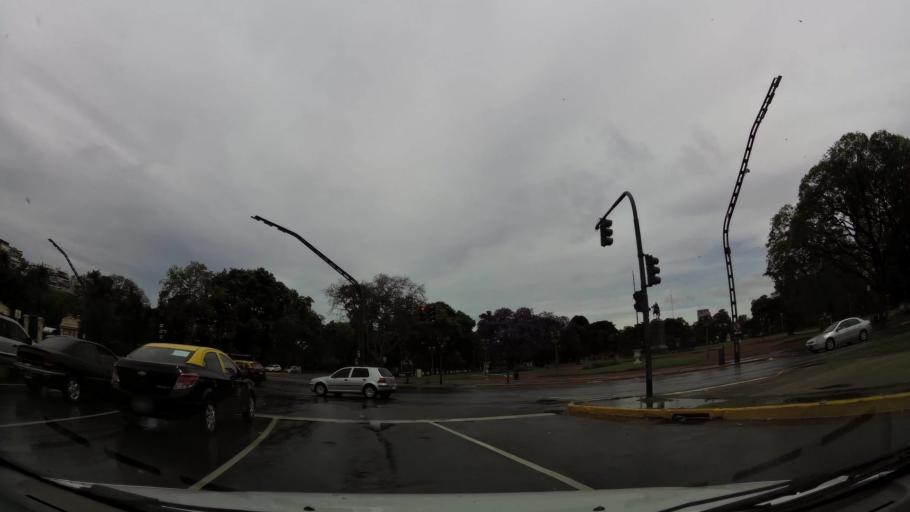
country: AR
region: Buenos Aires F.D.
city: Retiro
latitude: -34.5748
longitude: -58.4155
